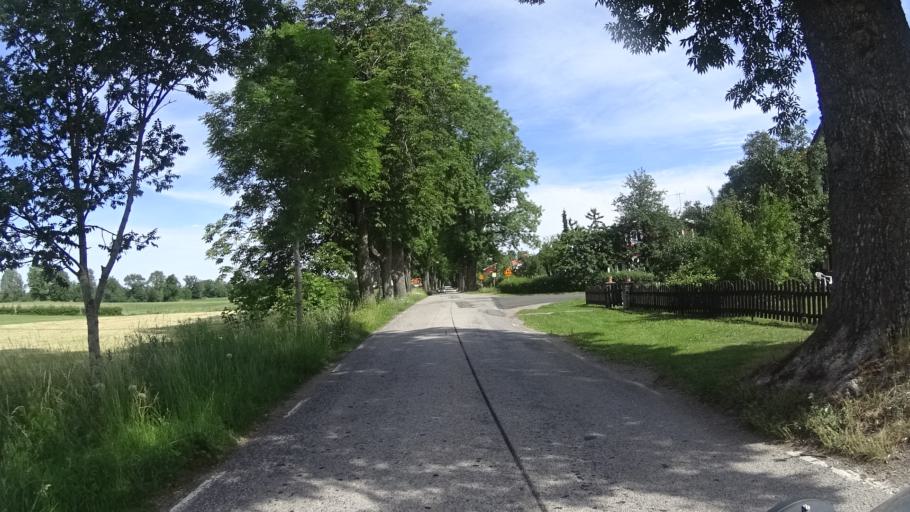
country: SE
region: Kalmar
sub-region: Vasterviks Kommun
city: Overum
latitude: 57.8919
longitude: 16.1696
